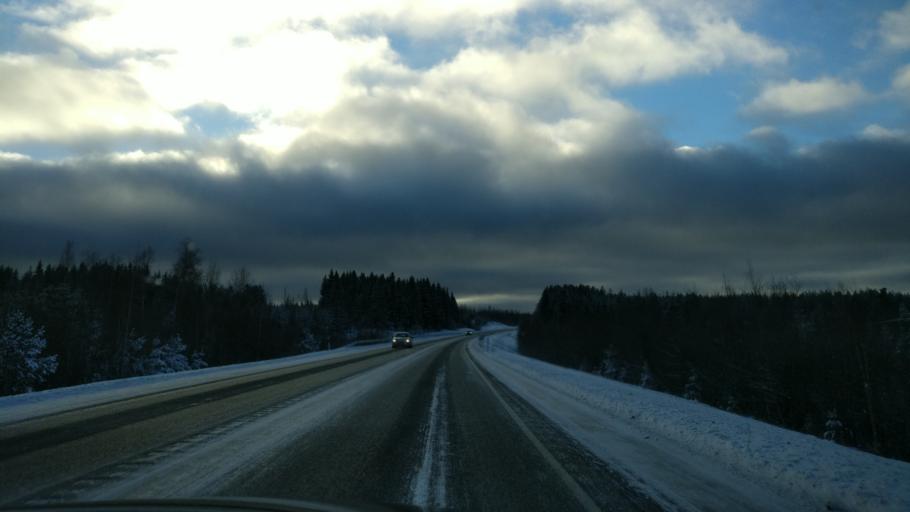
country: FI
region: Southern Savonia
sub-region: Mikkeli
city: Pertunmaa
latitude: 61.3987
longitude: 26.3858
